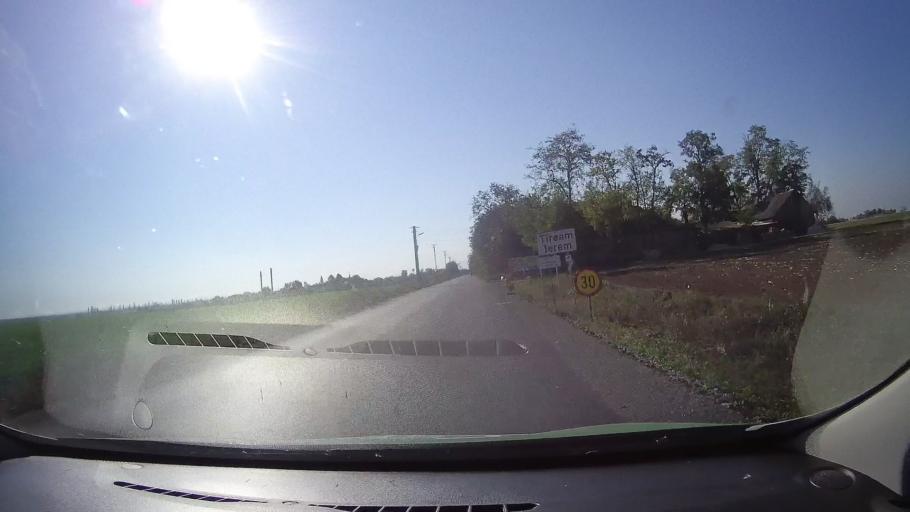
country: RO
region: Satu Mare
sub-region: Comuna Tiream
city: Tiream
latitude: 47.6228
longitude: 22.4680
